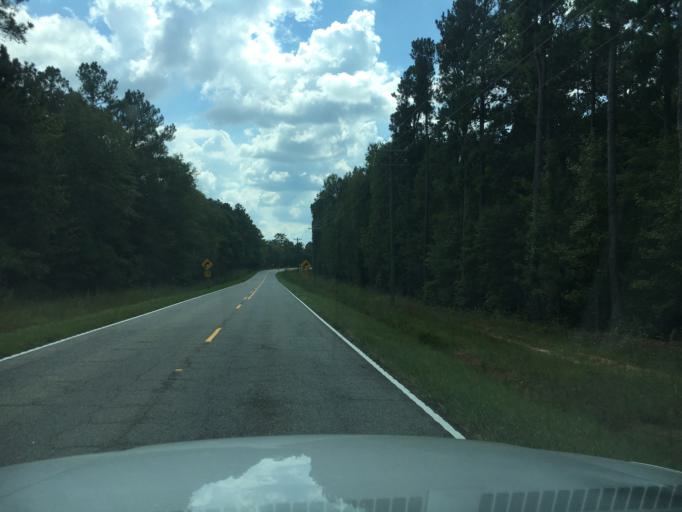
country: US
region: South Carolina
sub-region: Greenwood County
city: Greenwood
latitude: 34.0869
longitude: -82.1318
